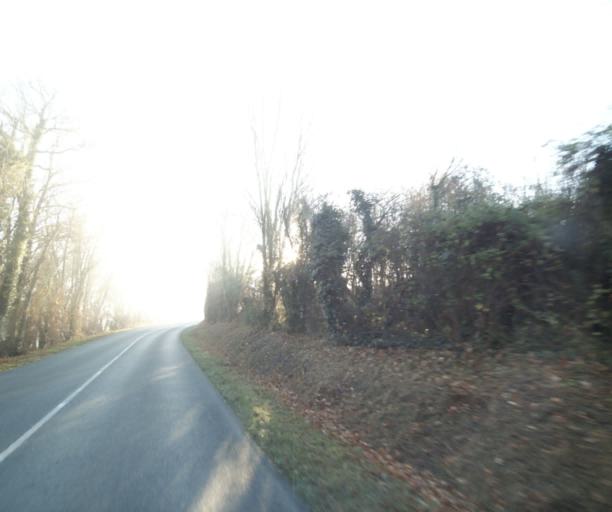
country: FR
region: Poitou-Charentes
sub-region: Departement de la Charente-Maritime
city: Bussac-sur-Charente
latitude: 45.7749
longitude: -0.6224
